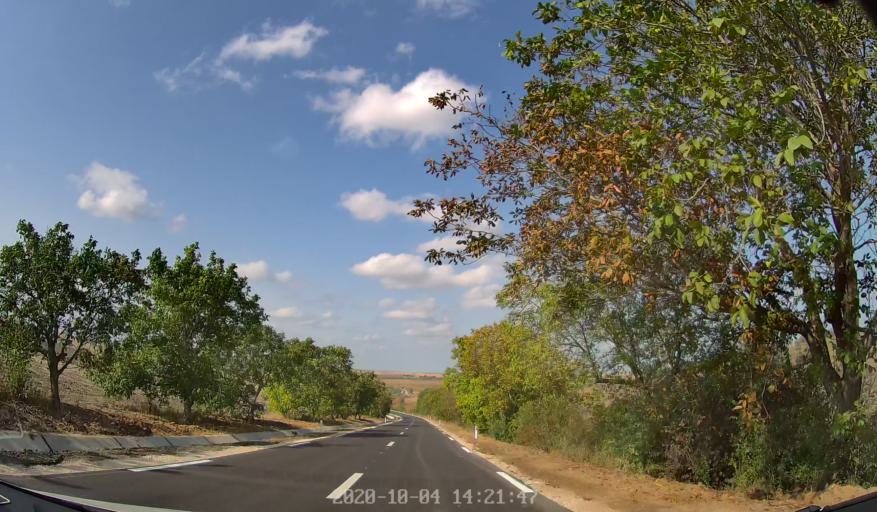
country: MD
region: Rezina
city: Saharna
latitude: 47.5893
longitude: 28.9535
